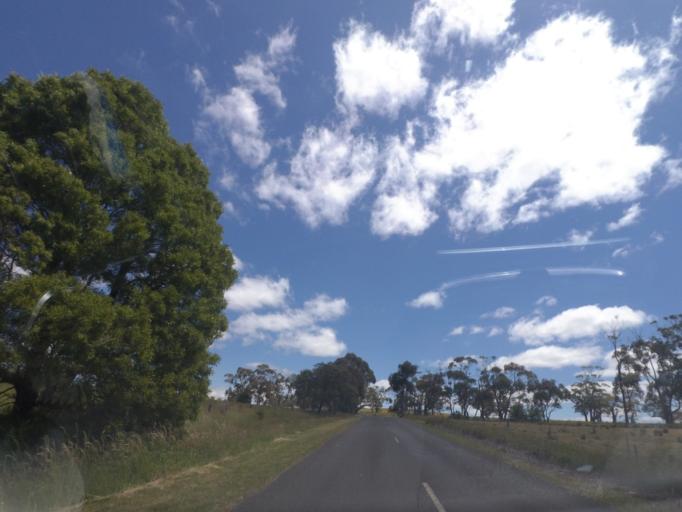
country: AU
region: Victoria
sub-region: Mount Alexander
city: Castlemaine
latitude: -37.3178
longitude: 144.1783
